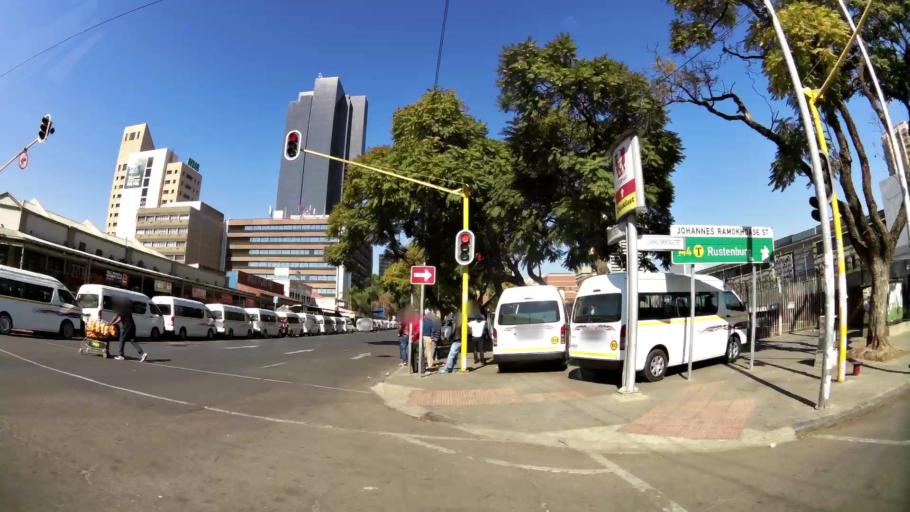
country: ZA
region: Gauteng
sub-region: City of Tshwane Metropolitan Municipality
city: Pretoria
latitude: -25.7431
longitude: 28.1949
